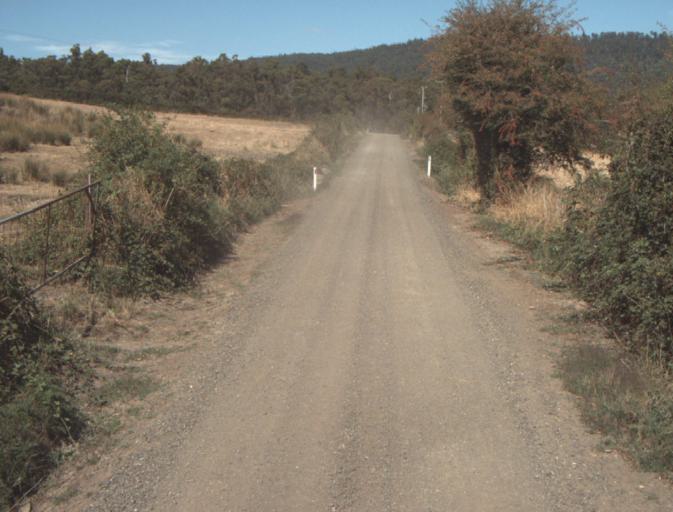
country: AU
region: Tasmania
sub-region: Launceston
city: Mayfield
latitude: -41.2578
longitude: 147.1693
